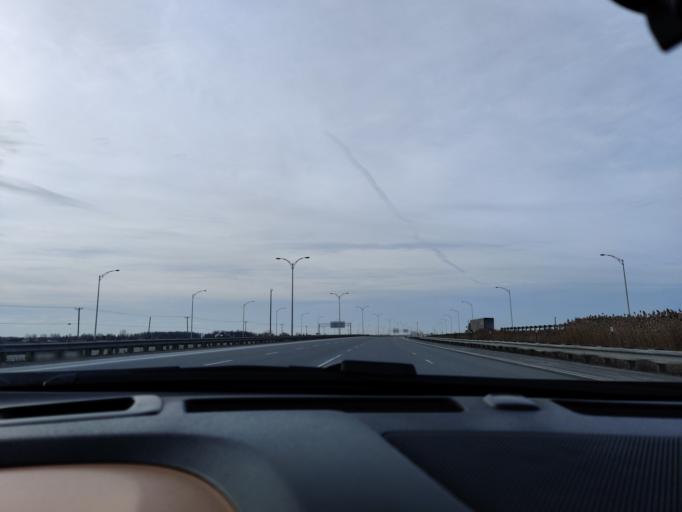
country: CA
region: Quebec
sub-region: Monteregie
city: Vaudreuil-Dorion
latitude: 45.3541
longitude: -74.0555
